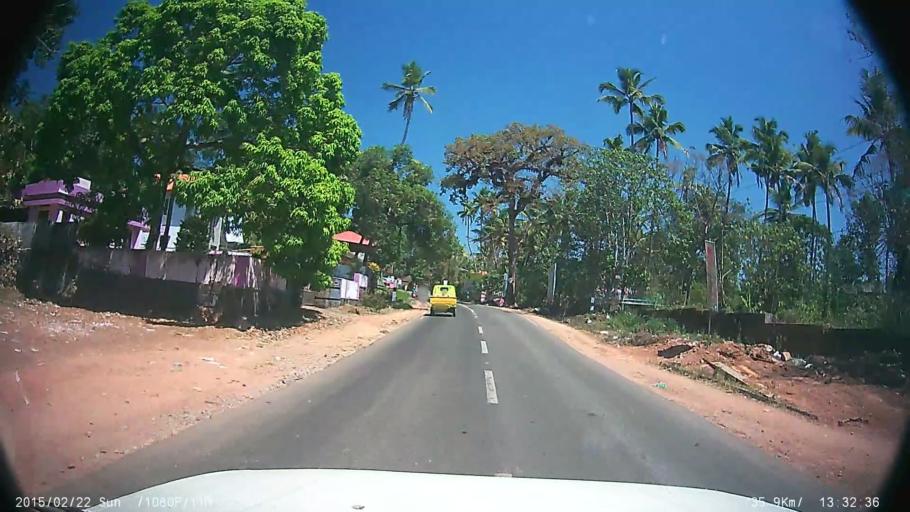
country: IN
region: Kerala
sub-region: Kottayam
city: Changanacheri
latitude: 9.4782
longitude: 76.5848
